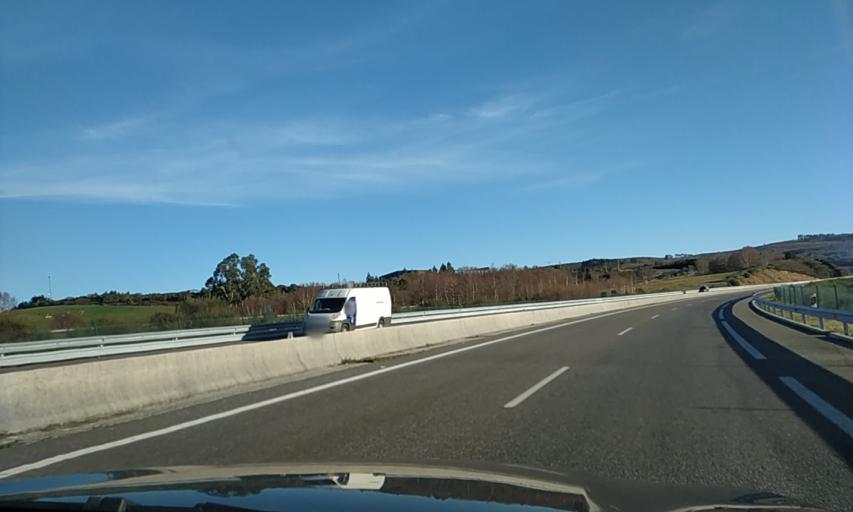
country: ES
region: Galicia
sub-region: Provincia de Pontevedra
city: Dozon
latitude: 42.5772
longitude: -8.0625
